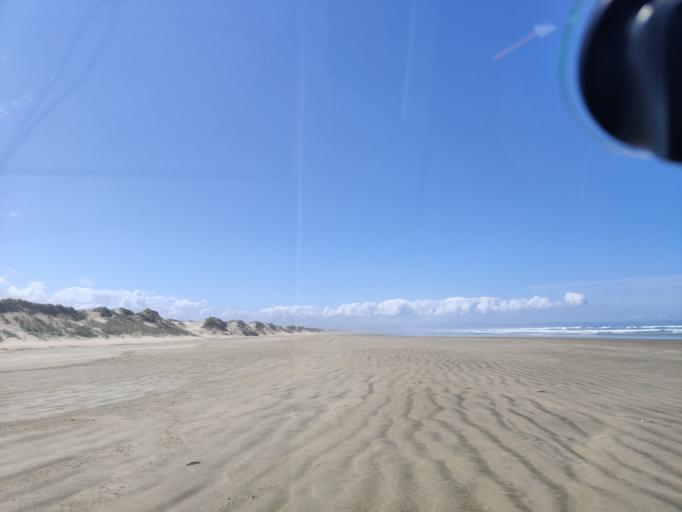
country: NZ
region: Northland
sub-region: Far North District
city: Kaitaia
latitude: -34.9180
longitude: 173.0986
